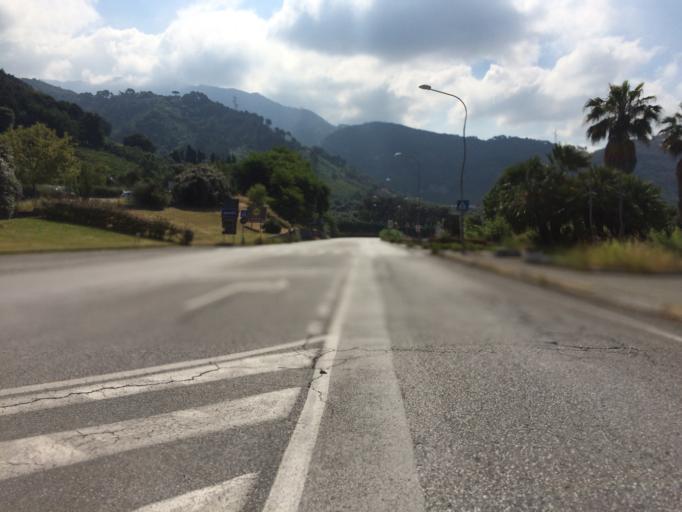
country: IT
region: Tuscany
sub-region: Provincia di Massa-Carrara
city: San Vito-Cerreto
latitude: 44.0184
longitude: 10.1525
